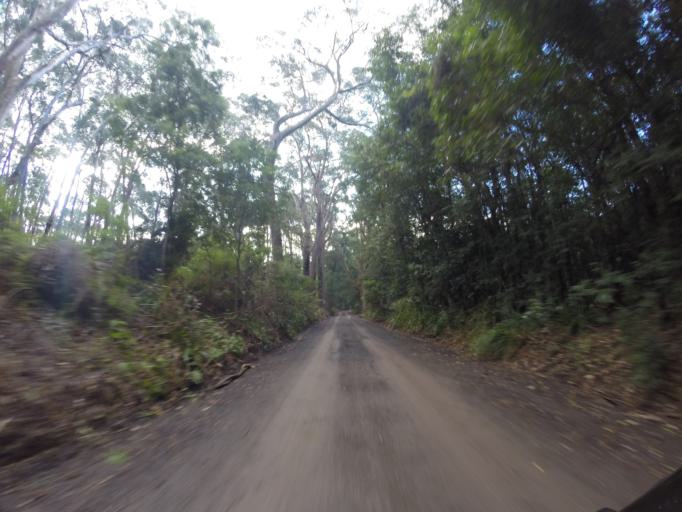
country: AU
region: New South Wales
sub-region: Wollongong
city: Cordeaux Heights
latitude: -34.4253
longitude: 150.7810
